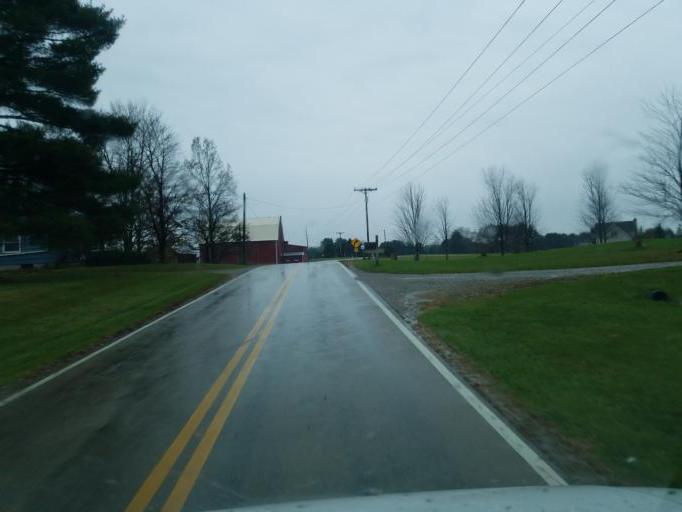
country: US
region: Ohio
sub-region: Delaware County
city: Sunbury
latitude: 40.3044
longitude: -82.8806
